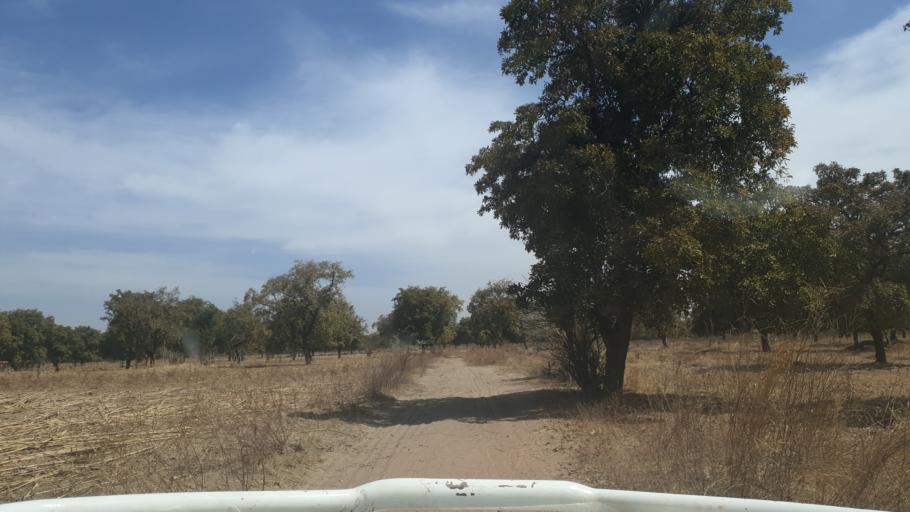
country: ML
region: Sikasso
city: Yorosso
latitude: 12.2877
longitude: -4.6745
